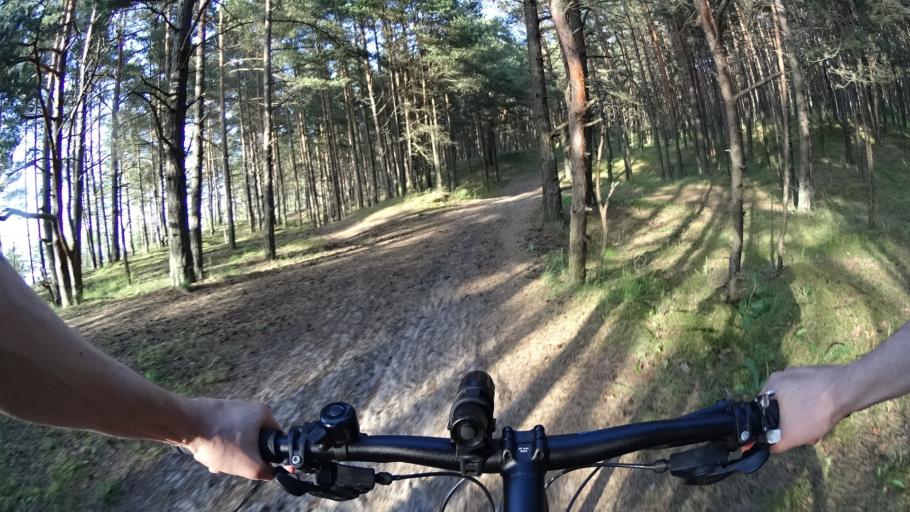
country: LV
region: Riga
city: Jaunciems
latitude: 57.0905
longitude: 24.1351
